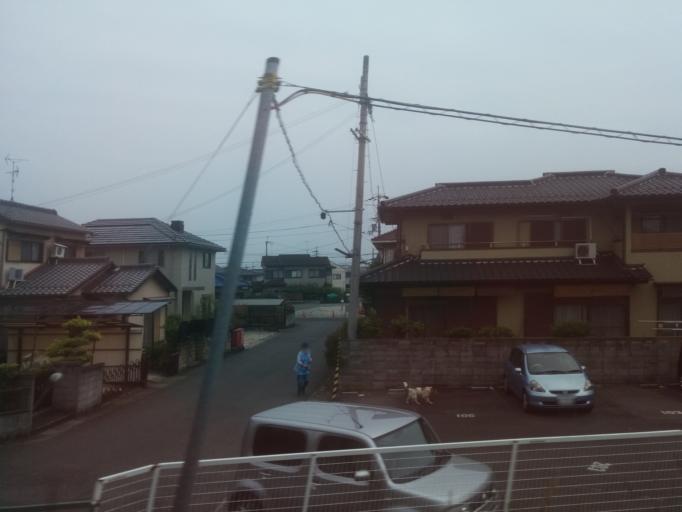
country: JP
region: Shiga Prefecture
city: Omihachiman
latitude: 35.1187
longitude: 136.0979
